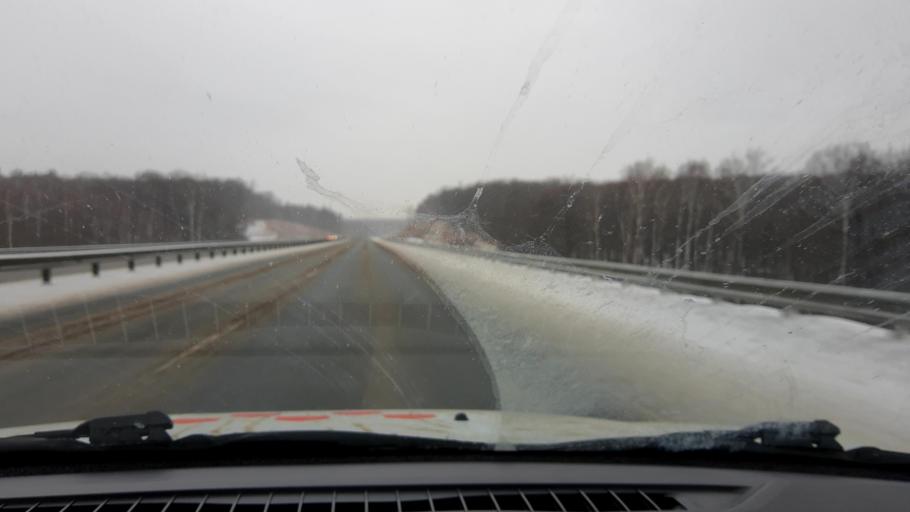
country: RU
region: Nizjnij Novgorod
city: Kstovo
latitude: 56.1009
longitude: 44.0377
